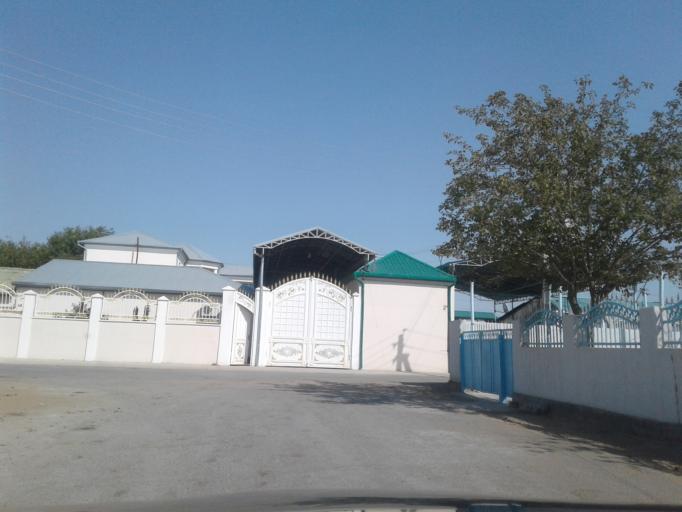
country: TM
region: Ahal
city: Ashgabat
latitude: 37.9731
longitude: 58.4373
